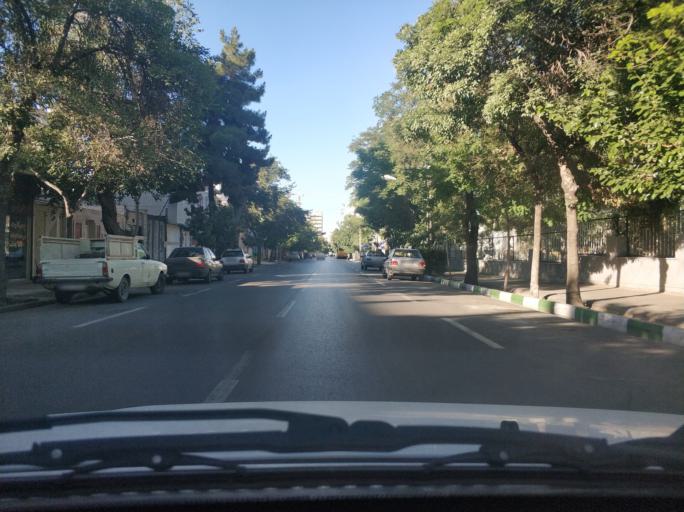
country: IR
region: Razavi Khorasan
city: Mashhad
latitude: 36.2779
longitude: 59.5946
